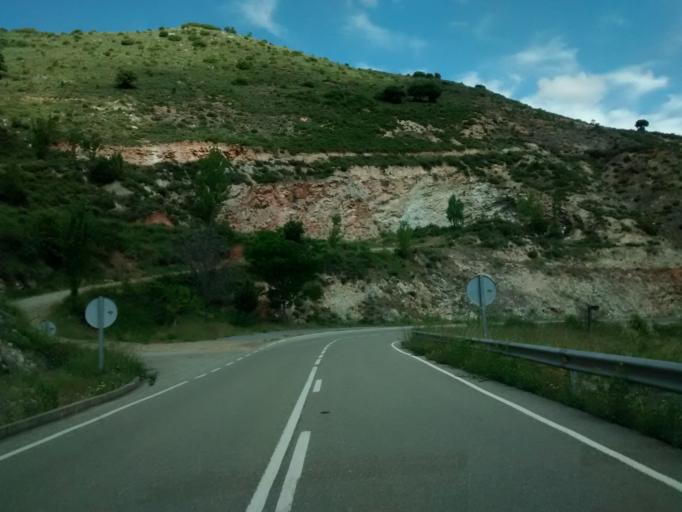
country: ES
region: La Rioja
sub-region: Provincia de La Rioja
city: Leza de Rio Leza
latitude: 42.3291
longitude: -2.4119
